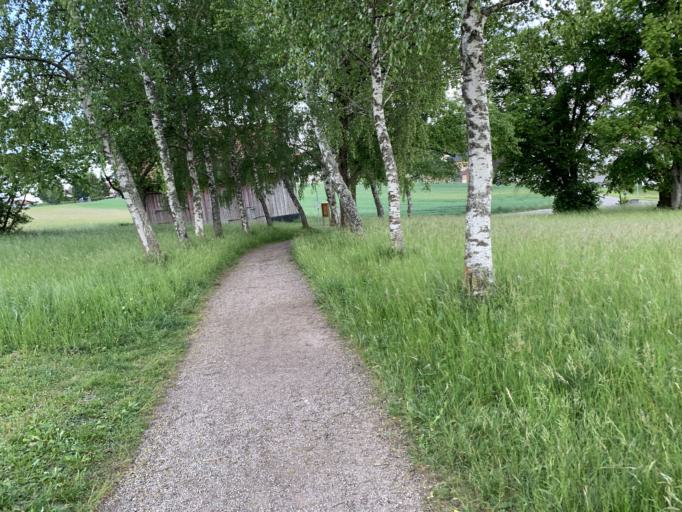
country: DE
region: Baden-Wuerttemberg
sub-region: Freiburg Region
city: Loffingen
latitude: 47.8903
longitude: 8.3417
